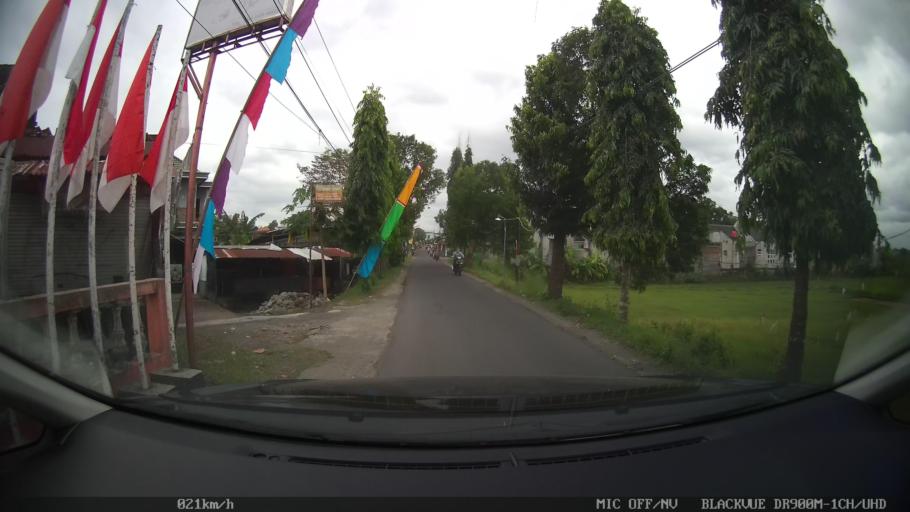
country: ID
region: Daerah Istimewa Yogyakarta
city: Depok
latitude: -7.8074
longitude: 110.4166
